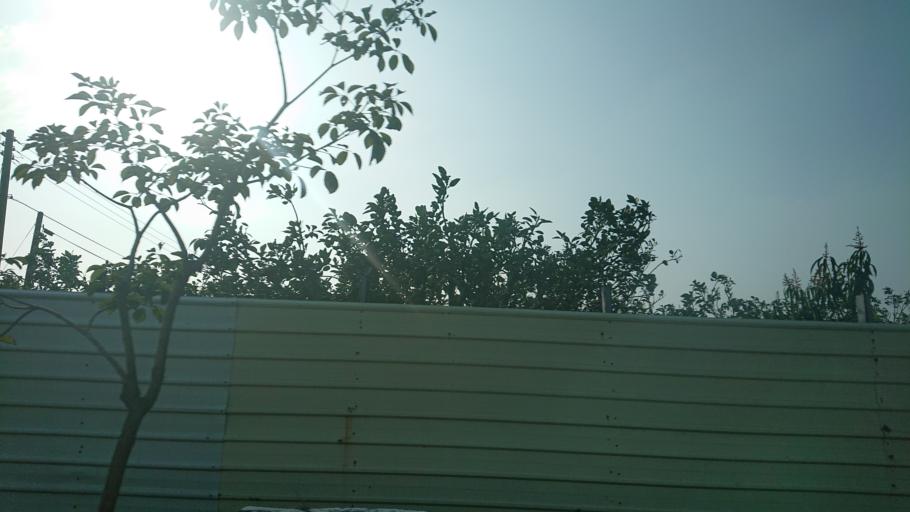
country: TW
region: Taiwan
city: Xinying
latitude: 23.2020
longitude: 120.2712
